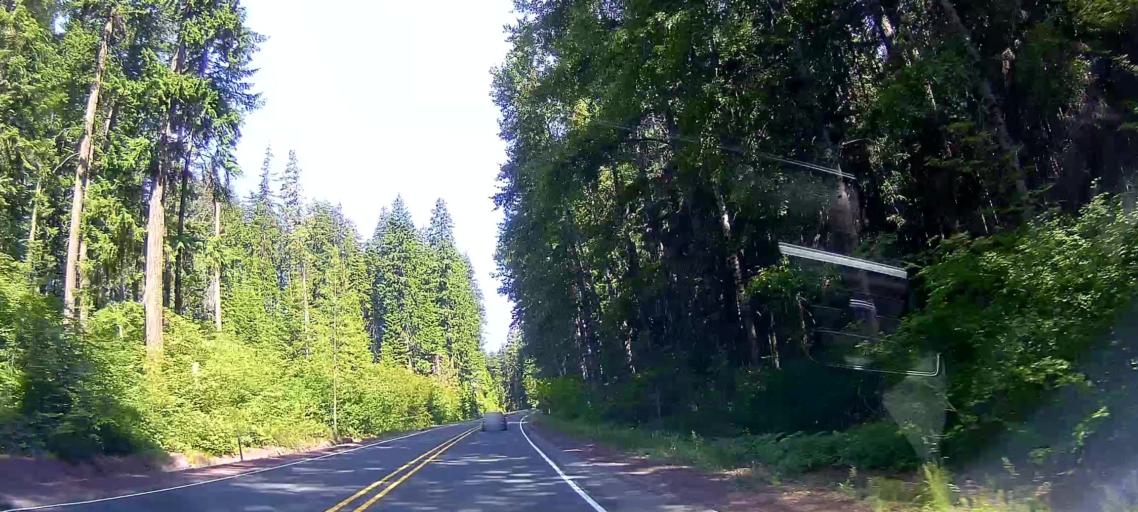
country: US
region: Oregon
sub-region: Jefferson County
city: Warm Springs
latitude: 45.1107
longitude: -121.5646
